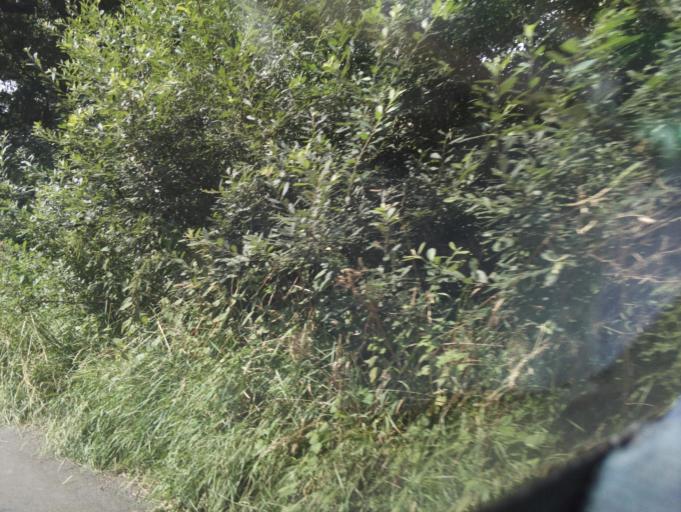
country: GB
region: England
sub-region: Wiltshire
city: Hankerton
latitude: 51.6085
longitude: -2.0493
